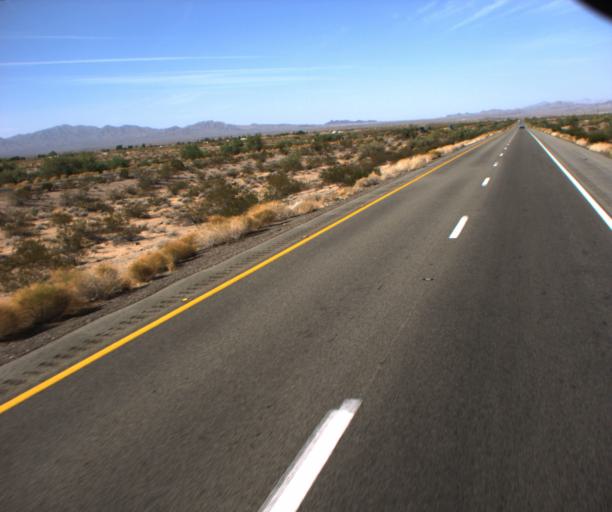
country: US
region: Arizona
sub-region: Mohave County
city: Desert Hills
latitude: 34.7668
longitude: -114.2004
